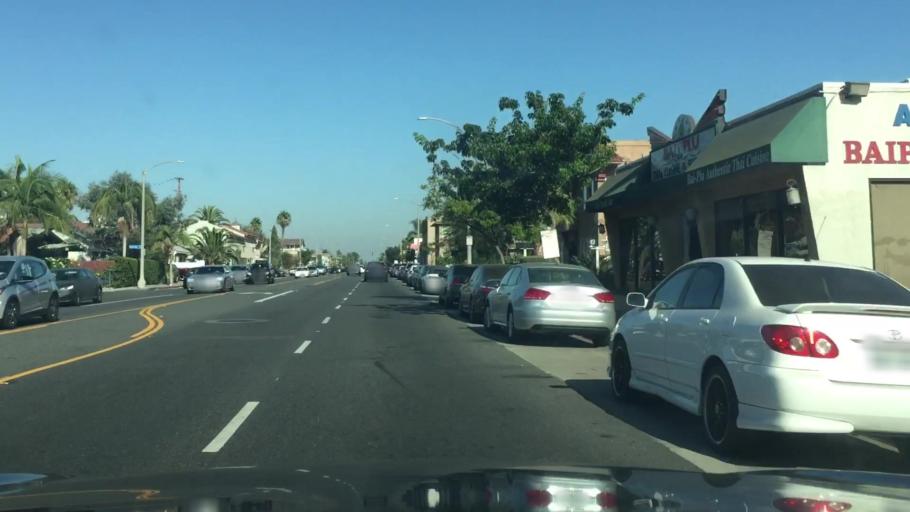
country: US
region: California
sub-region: Los Angeles County
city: Long Beach
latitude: 33.7752
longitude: -118.1715
